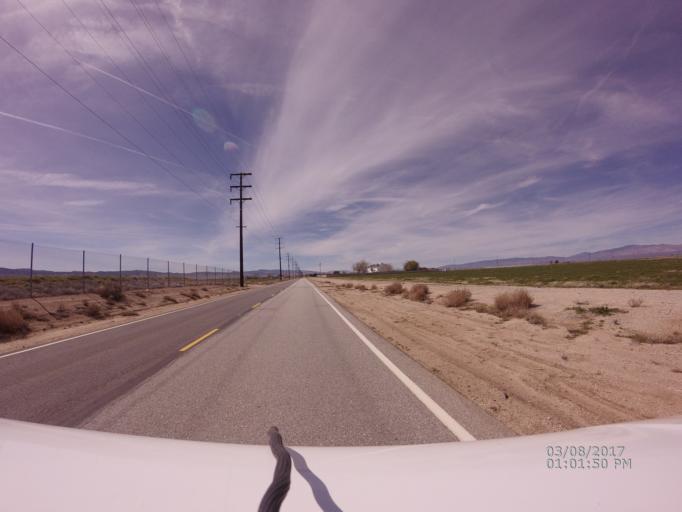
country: US
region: California
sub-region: Los Angeles County
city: Quartz Hill
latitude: 34.7185
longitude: -118.2636
